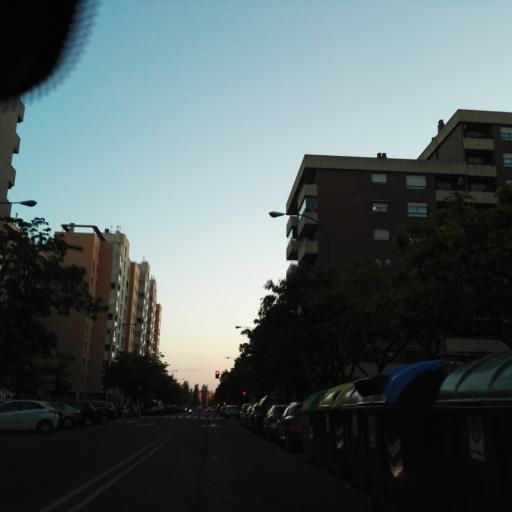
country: ES
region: Aragon
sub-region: Provincia de Zaragoza
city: Almozara
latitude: 41.6681
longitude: -0.8912
